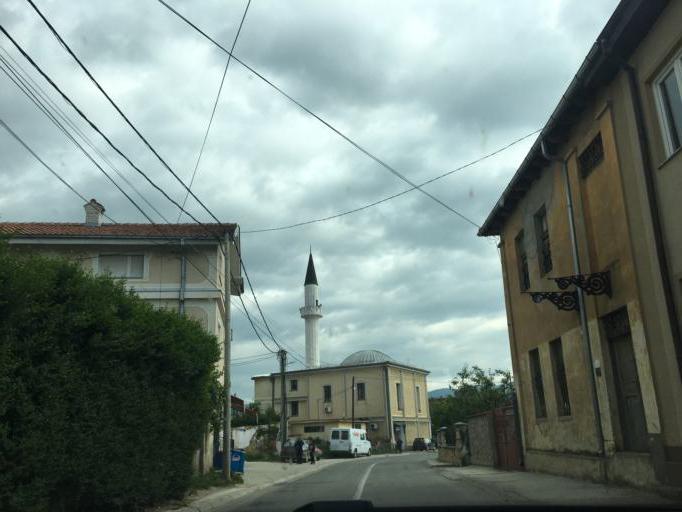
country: MK
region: Resen
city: Resen
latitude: 41.0920
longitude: 21.0108
